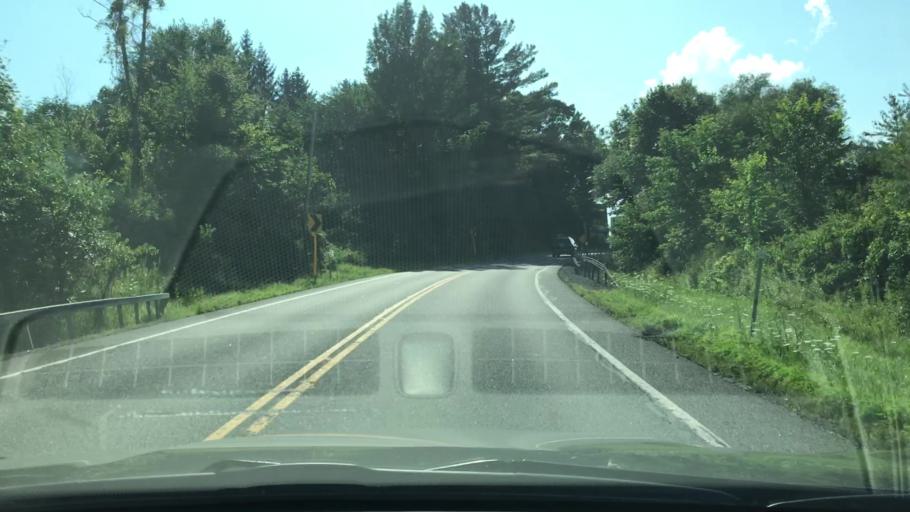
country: US
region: New York
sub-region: Warren County
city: Queensbury
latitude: 43.4040
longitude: -73.5399
